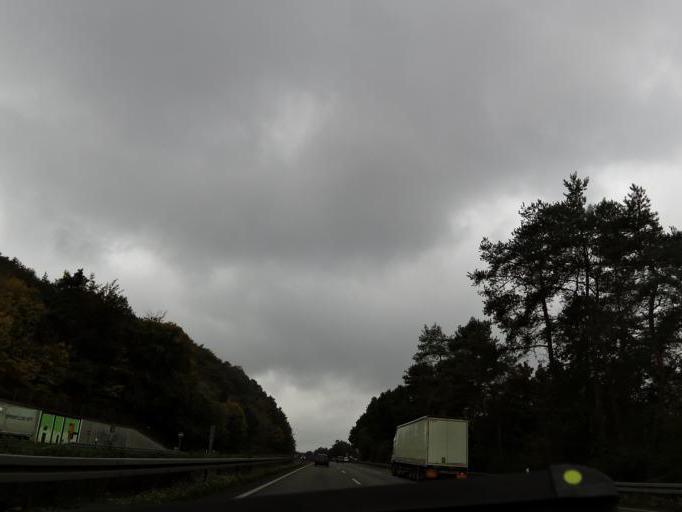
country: DE
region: Saarland
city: Sankt Ingbert
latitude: 49.2727
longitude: 7.1586
